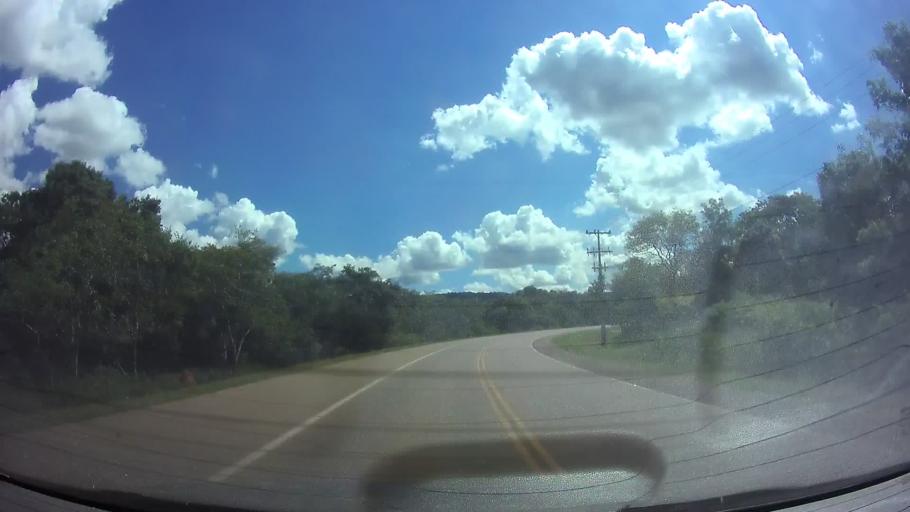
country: PY
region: Guaira
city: Itape
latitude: -25.9168
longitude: -56.7027
